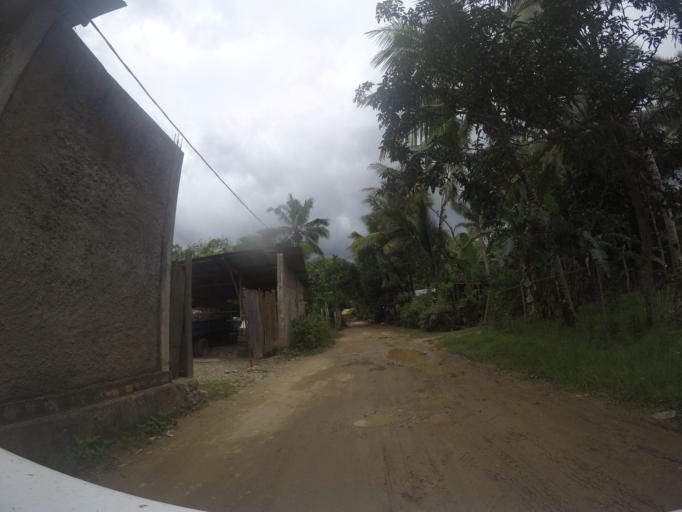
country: TL
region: Lautem
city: Lospalos
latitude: -8.5234
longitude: 126.9929
